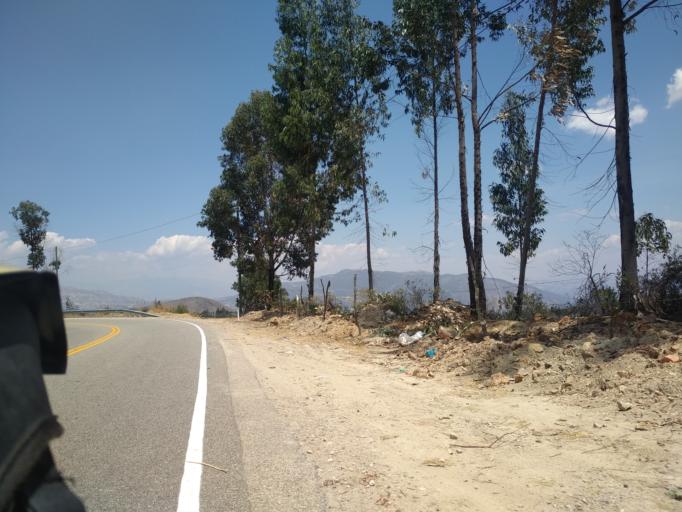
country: PE
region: Cajamarca
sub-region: San Marcos
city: San Marcos
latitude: -7.2861
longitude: -78.2098
